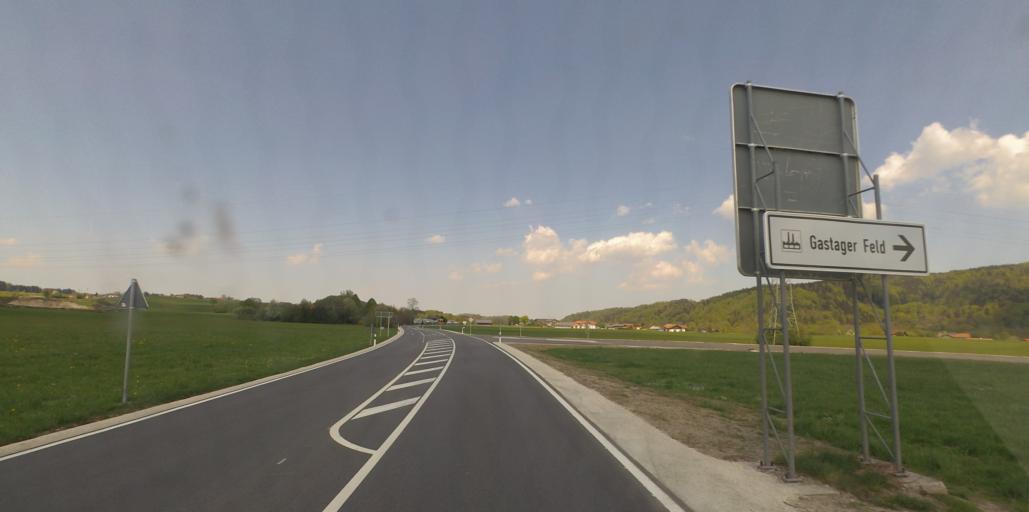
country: DE
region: Bavaria
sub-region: Upper Bavaria
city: Siegsdorf
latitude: 47.8323
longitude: 12.6354
